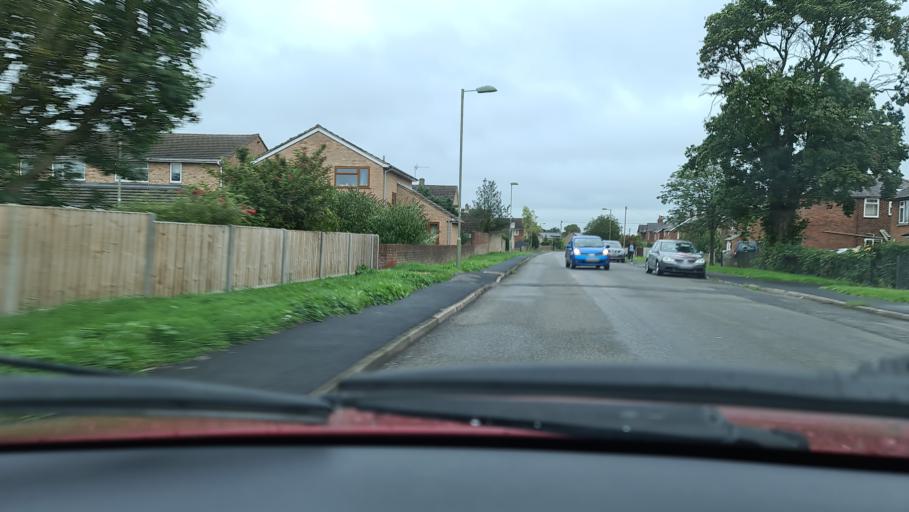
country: GB
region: England
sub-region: Oxfordshire
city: Bicester
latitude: 51.9069
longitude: -1.1648
